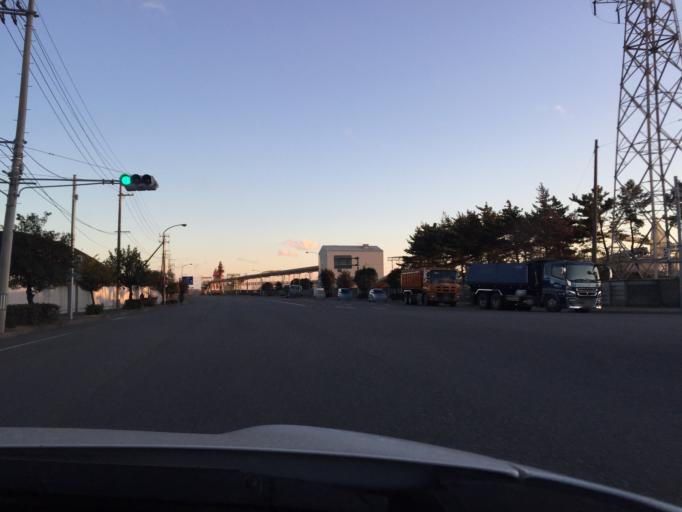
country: JP
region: Fukushima
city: Iwaki
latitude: 36.9396
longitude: 140.8778
